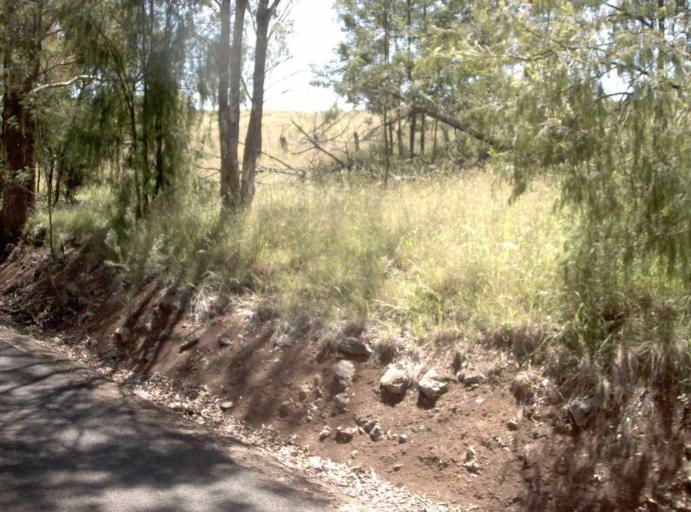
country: AU
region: Victoria
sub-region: East Gippsland
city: Lakes Entrance
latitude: -37.4304
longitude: 148.1988
